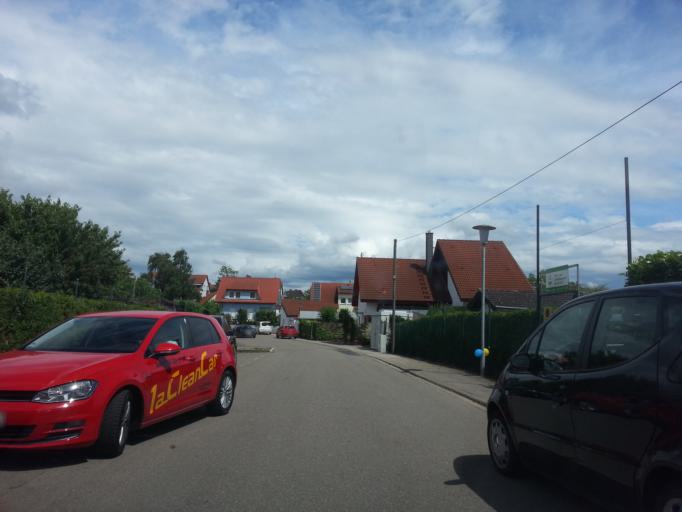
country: DE
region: Baden-Wuerttemberg
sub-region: Karlsruhe Region
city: Ketsch
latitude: 49.3593
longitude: 8.5248
